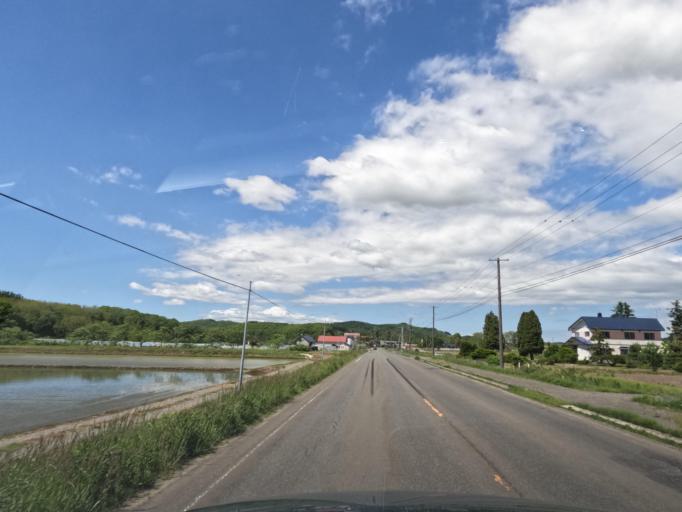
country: JP
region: Hokkaido
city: Iwamizawa
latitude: 43.1394
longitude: 141.8056
